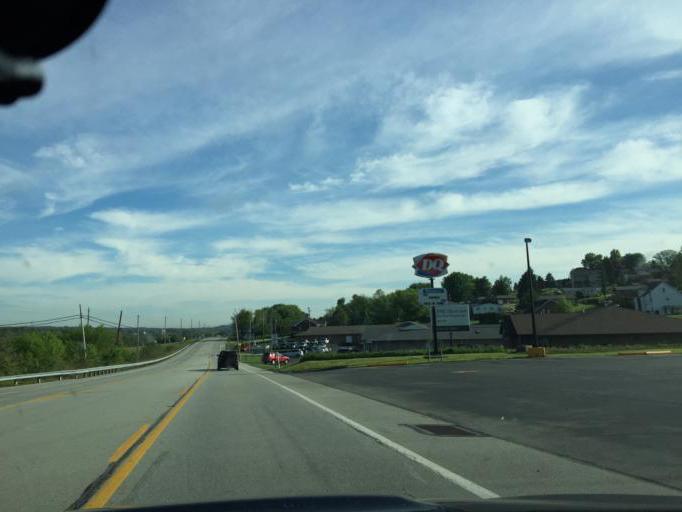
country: US
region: Pennsylvania
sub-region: Westmoreland County
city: Lawson Heights
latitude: 40.2891
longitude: -79.3939
